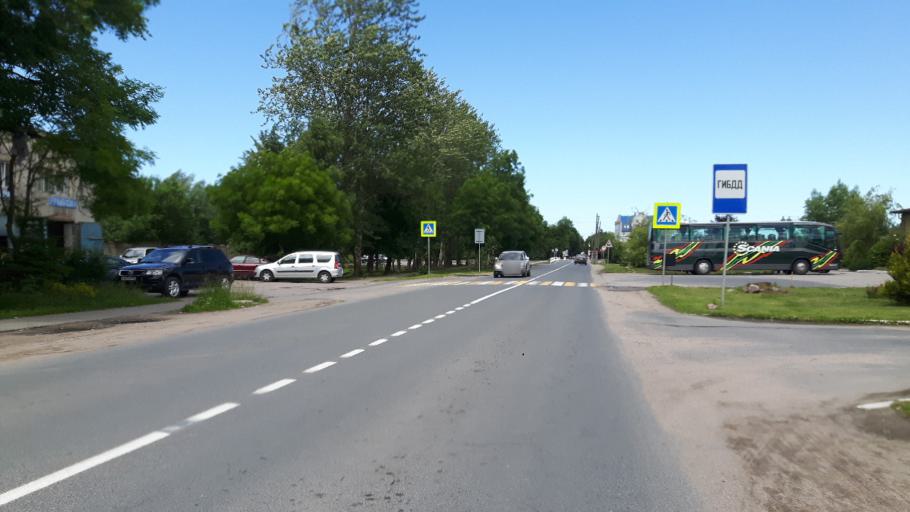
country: RU
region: Kaliningrad
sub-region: Zelenogradskiy Rayon
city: Zelenogradsk
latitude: 54.9509
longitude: 20.4703
